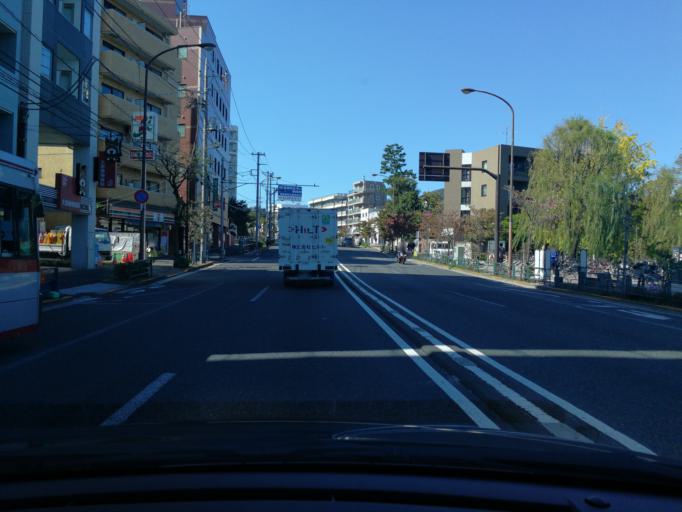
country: JP
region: Kanagawa
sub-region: Kawasaki-shi
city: Kawasaki
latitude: 35.6001
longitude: 139.6909
